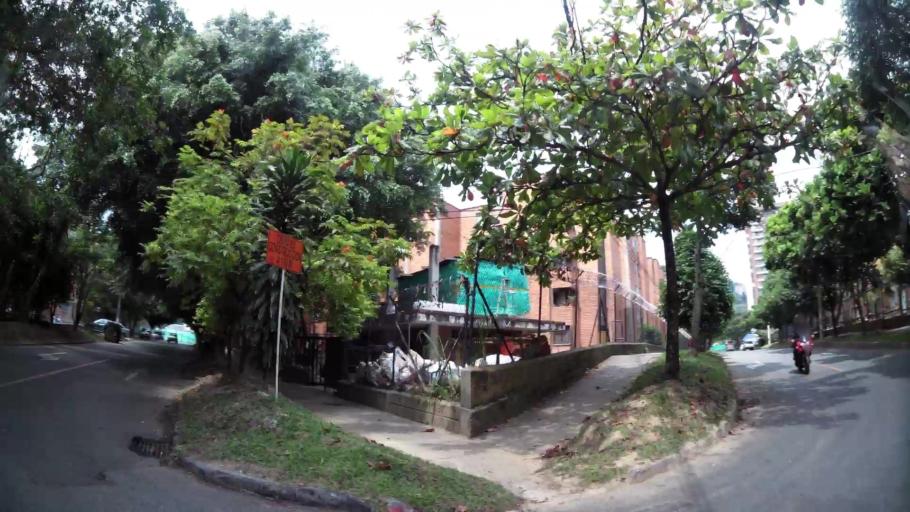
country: CO
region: Antioquia
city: Itagui
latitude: 6.1959
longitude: -75.5937
